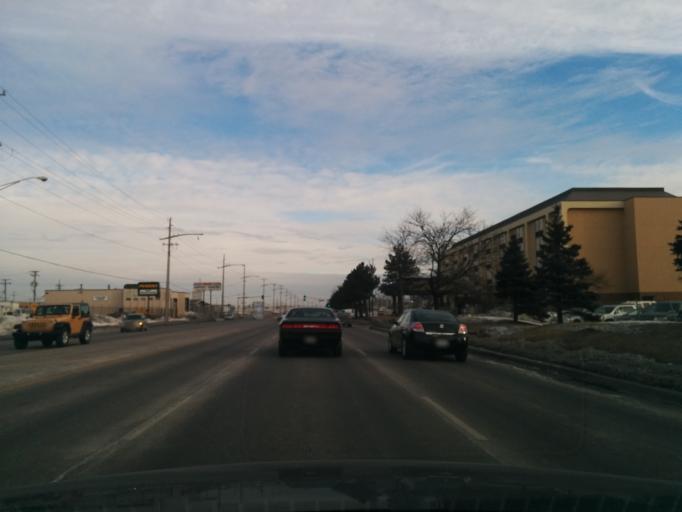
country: US
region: Illinois
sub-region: Cook County
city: Schiller Park
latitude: 41.9488
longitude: -87.8855
